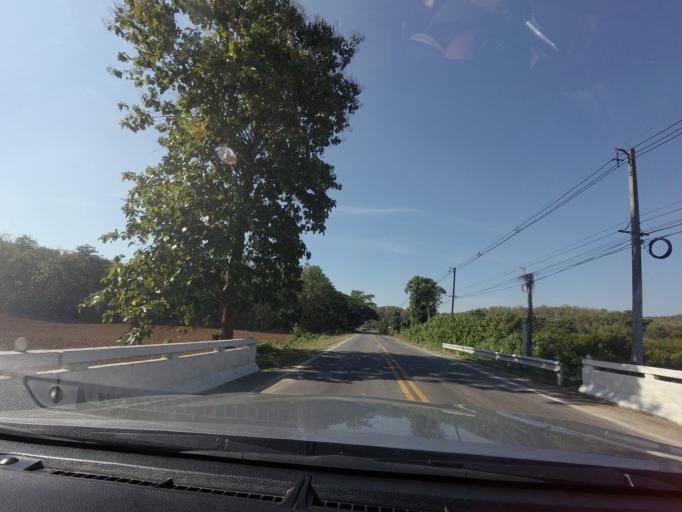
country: TH
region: Sukhothai
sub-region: Amphoe Si Satchanalai
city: Si Satchanalai
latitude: 17.6295
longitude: 99.6995
